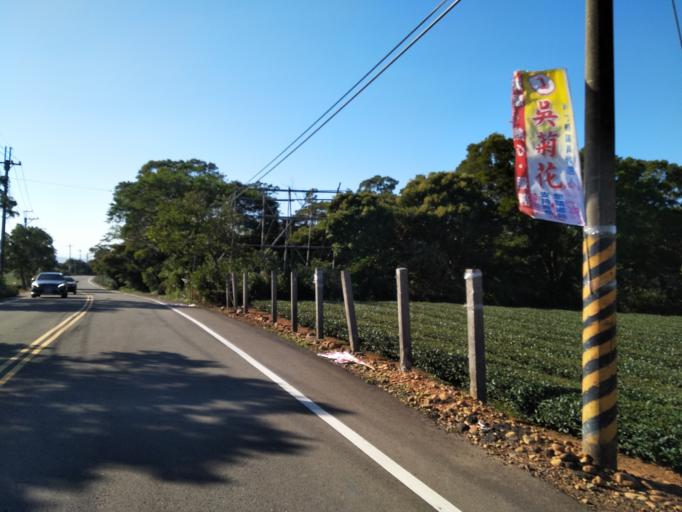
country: TW
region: Taiwan
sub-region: Hsinchu
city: Zhubei
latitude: 24.8690
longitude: 121.0908
